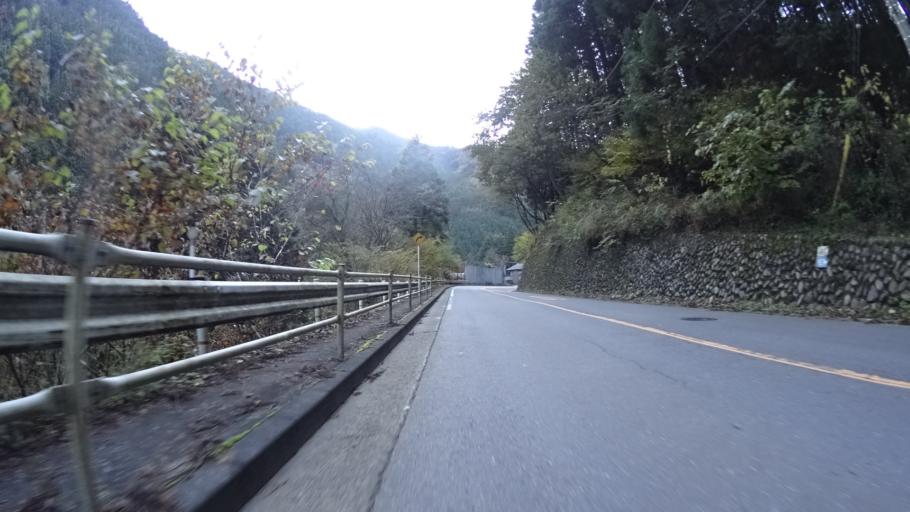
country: JP
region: Tokyo
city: Itsukaichi
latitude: 35.7168
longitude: 139.1512
